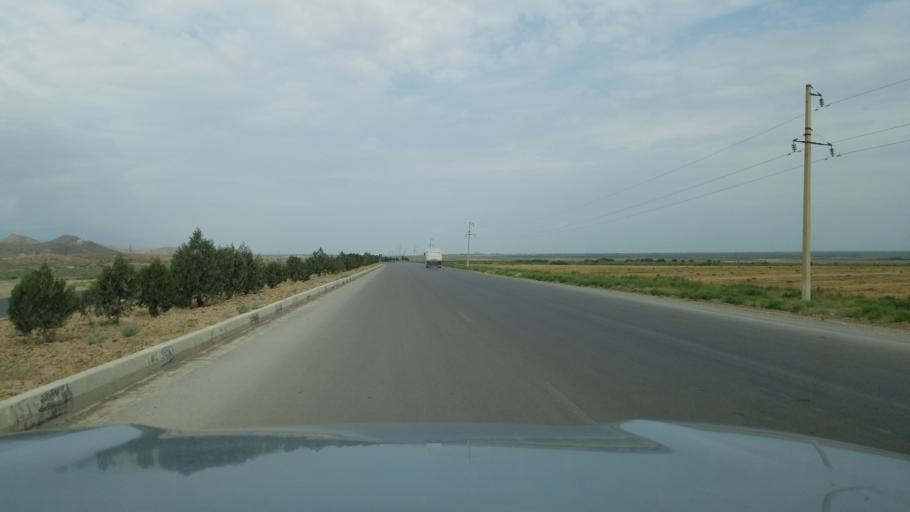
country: TM
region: Ahal
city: Baharly
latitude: 38.2401
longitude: 57.7683
